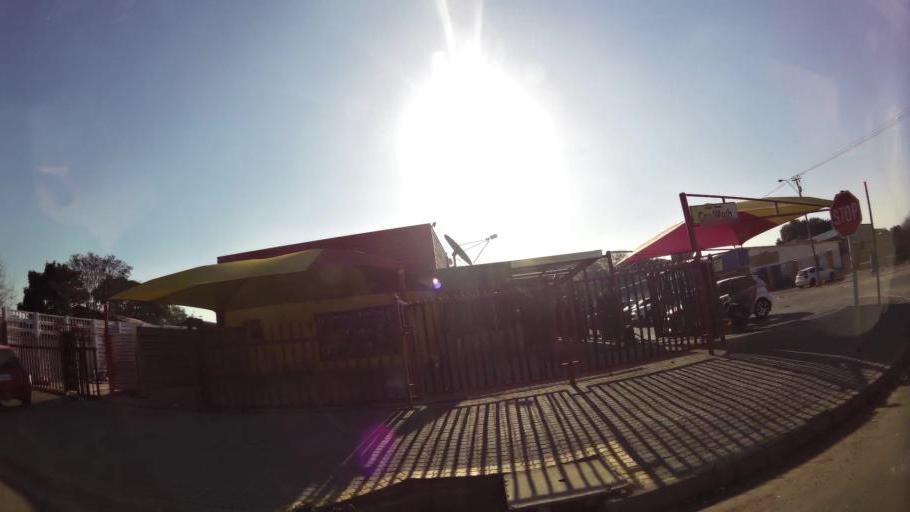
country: ZA
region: North-West
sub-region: Bojanala Platinum District Municipality
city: Rustenburg
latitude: -25.6544
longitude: 27.2353
